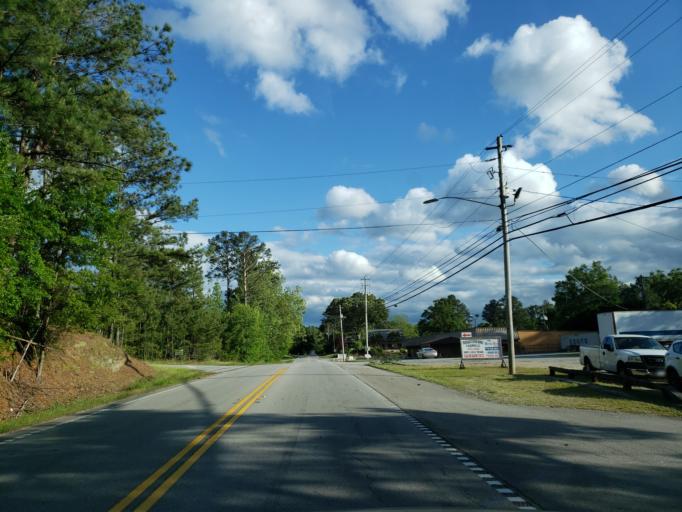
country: US
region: Georgia
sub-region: Haralson County
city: Tallapoosa
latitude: 33.7618
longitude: -85.2941
